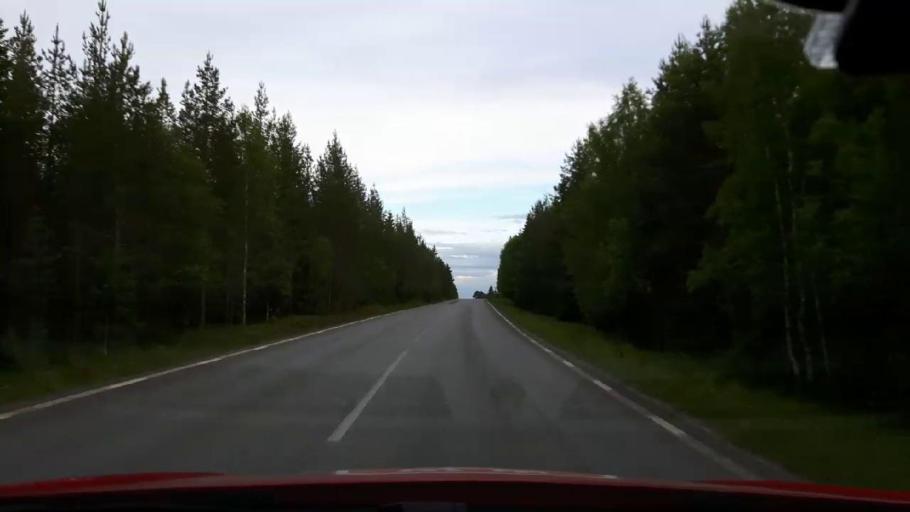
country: SE
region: Jaemtland
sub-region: OEstersunds Kommun
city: Ostersund
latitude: 63.0689
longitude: 14.4474
